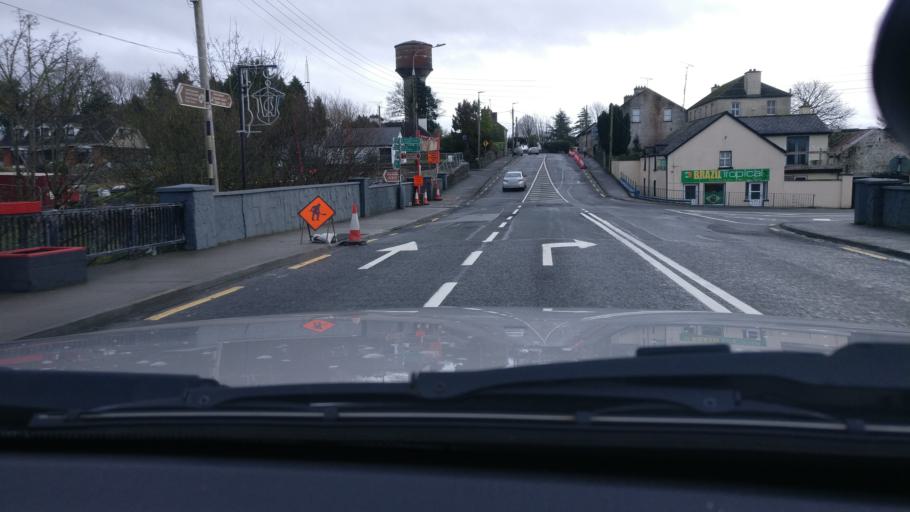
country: IE
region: Leinster
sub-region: An Longfort
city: Ballymahon
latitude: 53.5618
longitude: -7.7620
